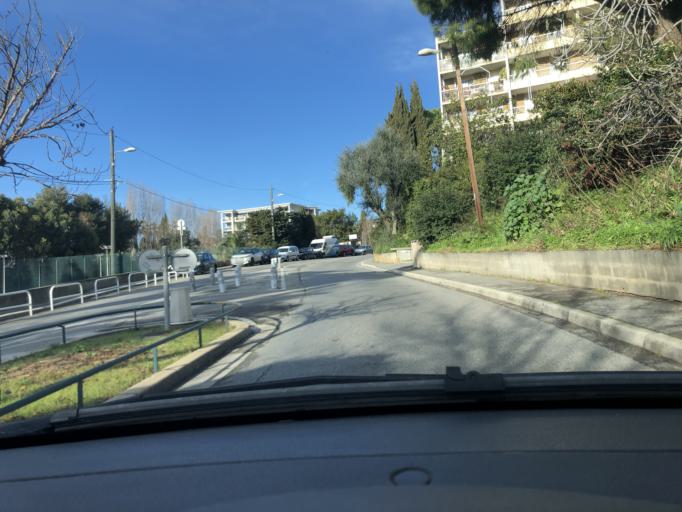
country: FR
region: Provence-Alpes-Cote d'Azur
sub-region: Departement des Alpes-Maritimes
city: Saint-Laurent-du-Var
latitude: 43.6778
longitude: 7.2149
